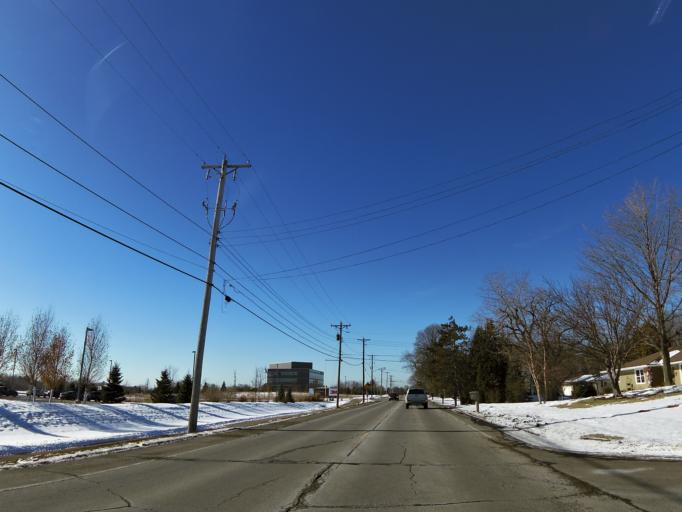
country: US
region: Minnesota
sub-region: Ramsey County
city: Maplewood
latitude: 44.9631
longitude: -92.9992
